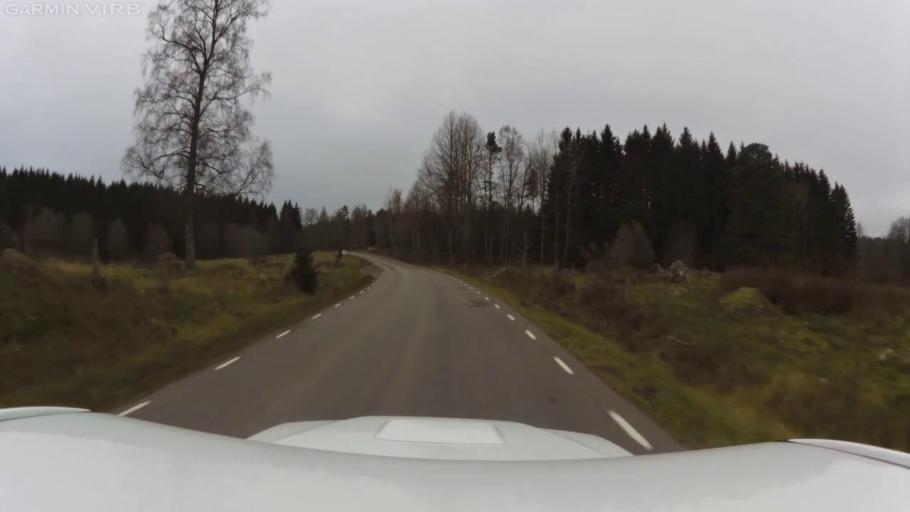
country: SE
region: OEstergoetland
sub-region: Linkopings Kommun
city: Vikingstad
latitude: 58.2295
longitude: 15.3956
